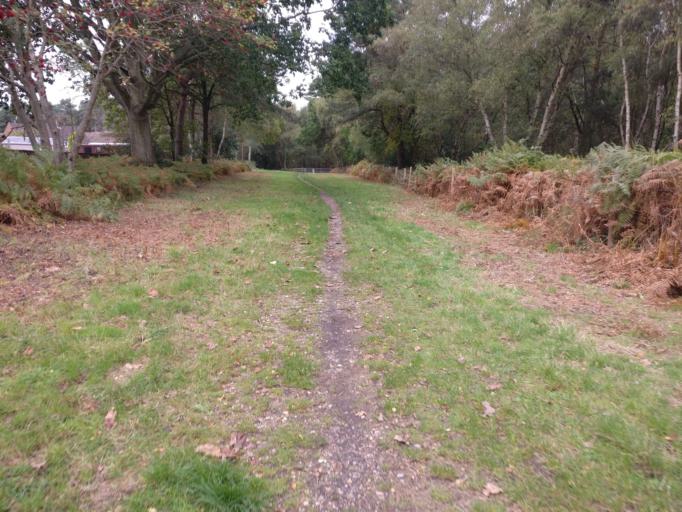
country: GB
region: England
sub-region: Surrey
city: Camberley
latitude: 51.3504
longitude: -0.7293
